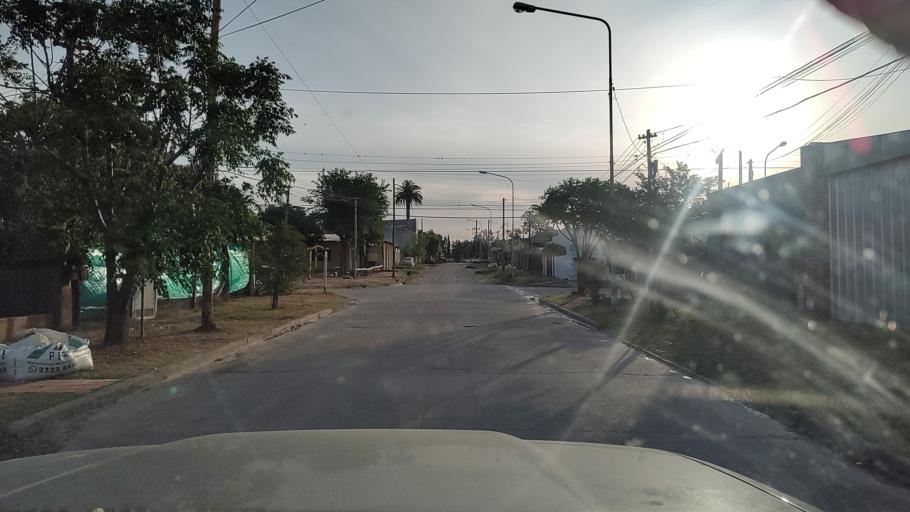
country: AR
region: Buenos Aires
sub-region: Partido de Lujan
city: Lujan
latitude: -34.5699
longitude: -59.1329
